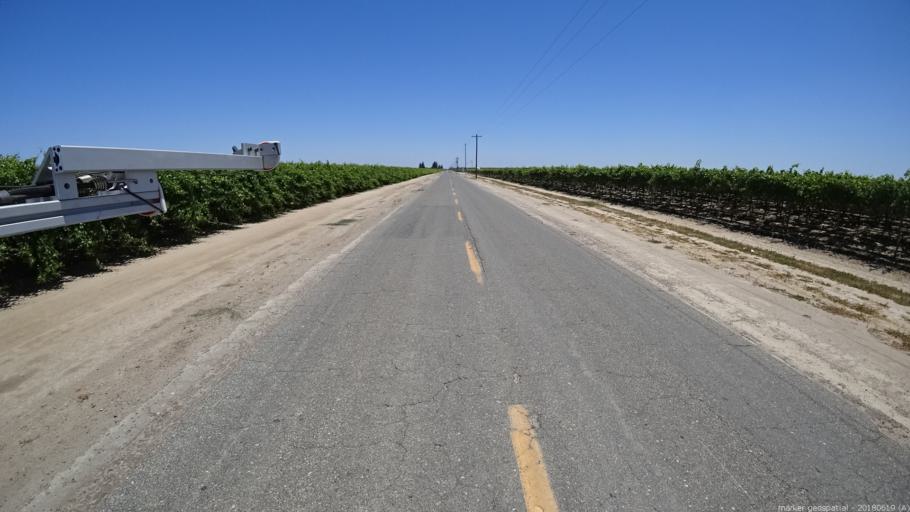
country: US
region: California
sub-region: Madera County
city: Parkwood
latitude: 36.8658
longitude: -120.0818
